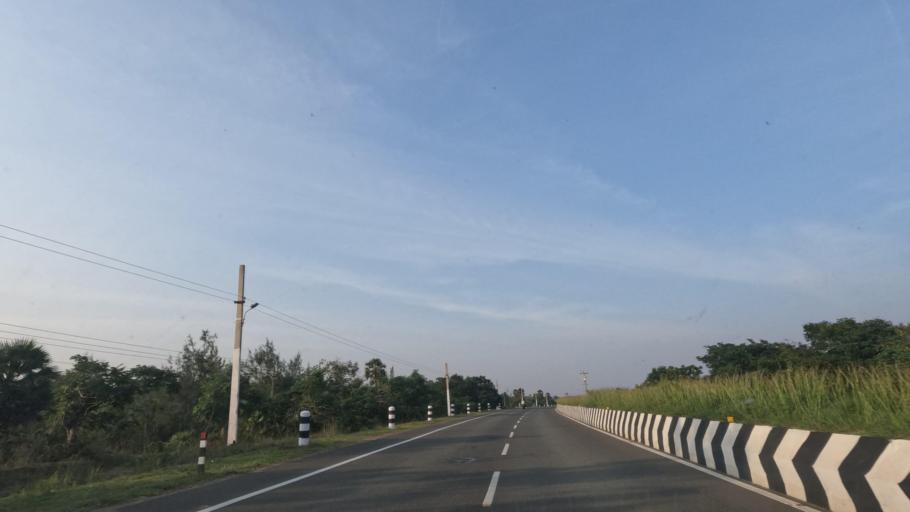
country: IN
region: Tamil Nadu
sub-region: Kancheepuram
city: Mamallapuram
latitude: 12.6746
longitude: 80.2119
